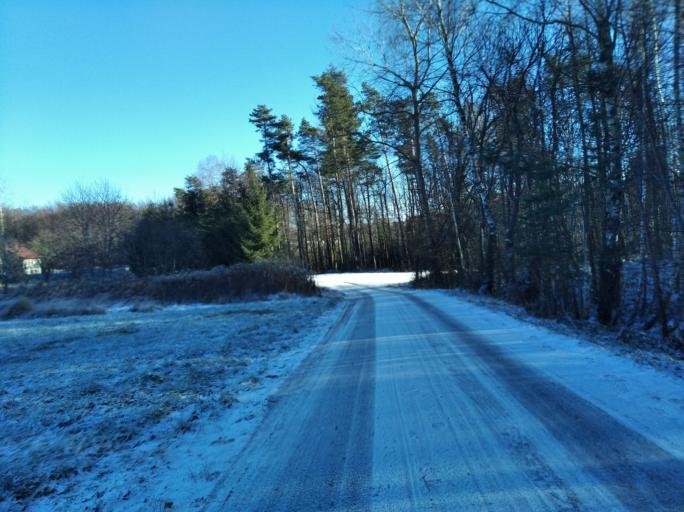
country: PL
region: Subcarpathian Voivodeship
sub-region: Powiat ropczycko-sedziszowski
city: Iwierzyce
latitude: 49.9680
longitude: 21.7377
